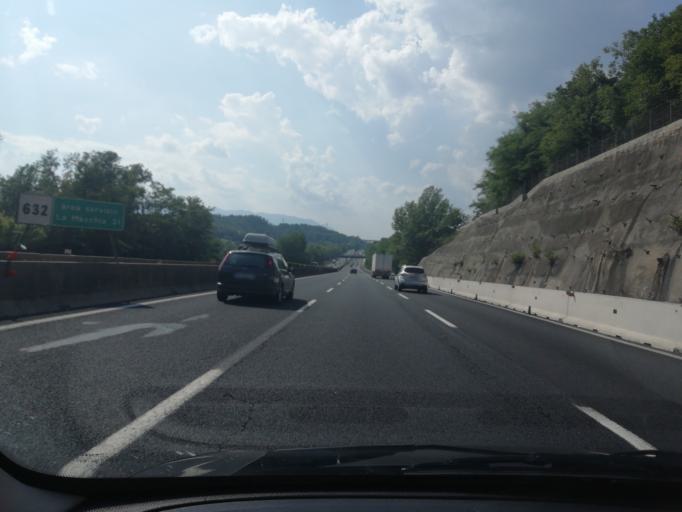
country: IT
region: Latium
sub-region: Provincia di Frosinone
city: Arnara
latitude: 41.5741
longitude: 13.3743
